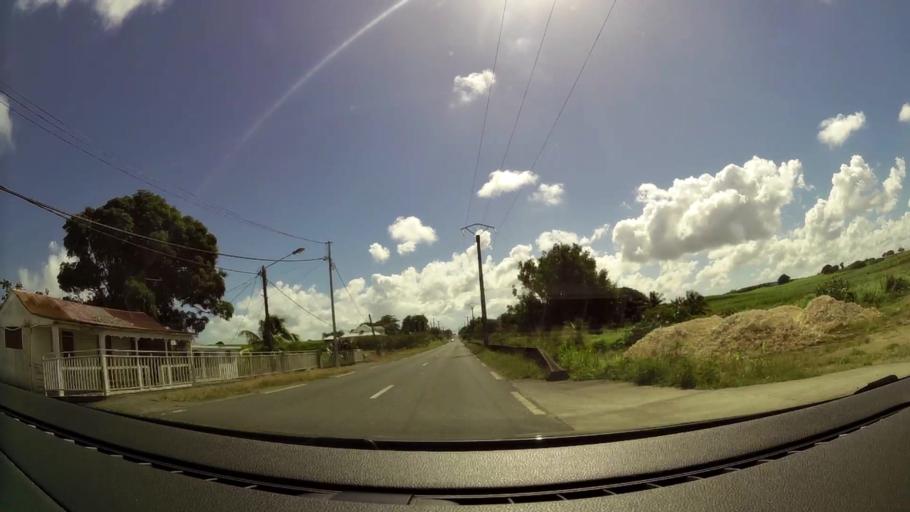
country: GP
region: Guadeloupe
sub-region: Guadeloupe
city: Petit-Canal
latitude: 16.4124
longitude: -61.4699
